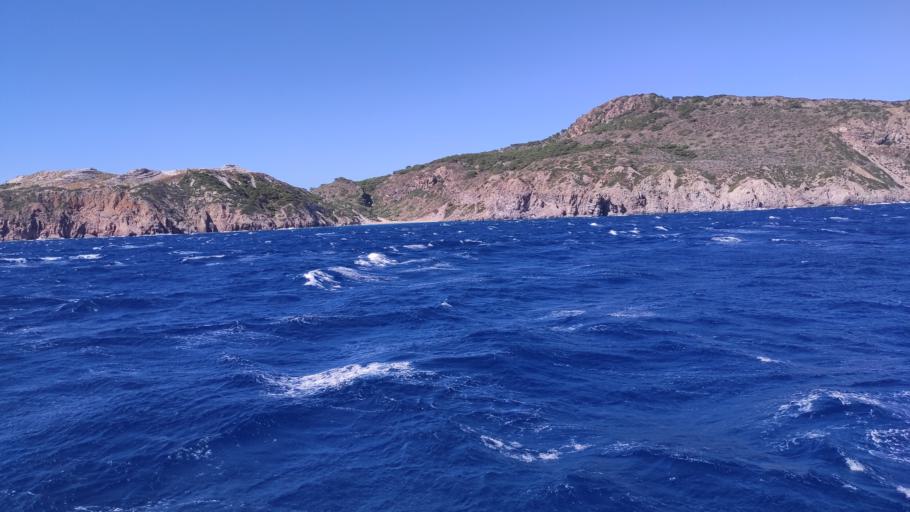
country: GR
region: South Aegean
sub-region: Nomos Dodekanisou
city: Mandraki
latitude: 36.6775
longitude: 27.1472
